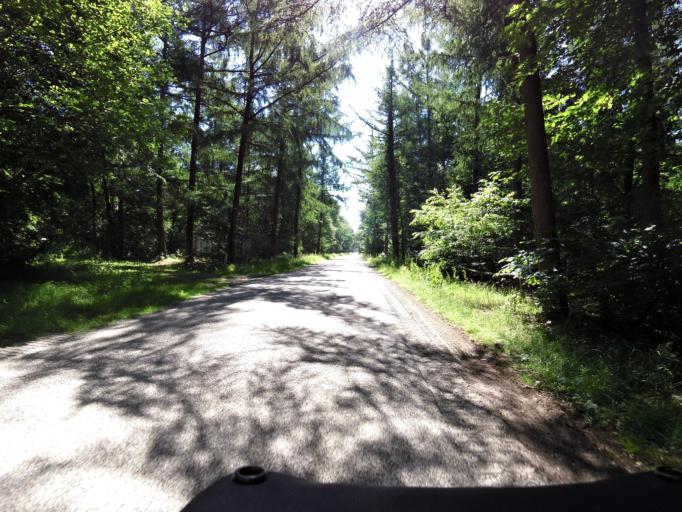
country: NL
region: Overijssel
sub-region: Gemeente Twenterand
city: Den Ham
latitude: 52.5413
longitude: 6.4839
